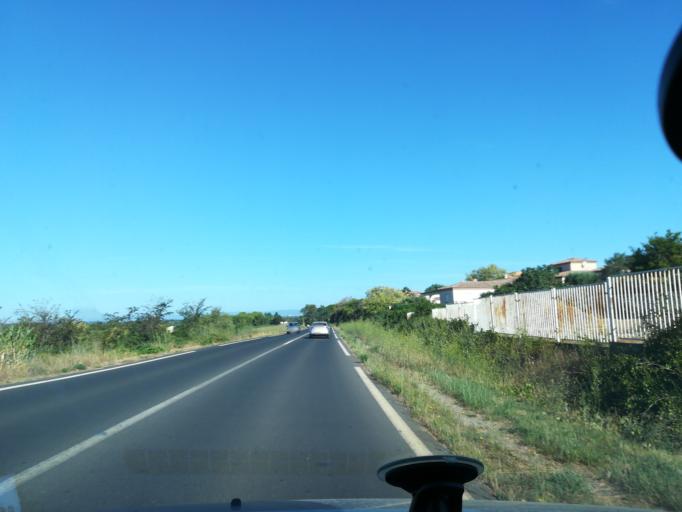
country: FR
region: Languedoc-Roussillon
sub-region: Departement de l'Herault
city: Portiragnes
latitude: 43.2981
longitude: 3.3427
